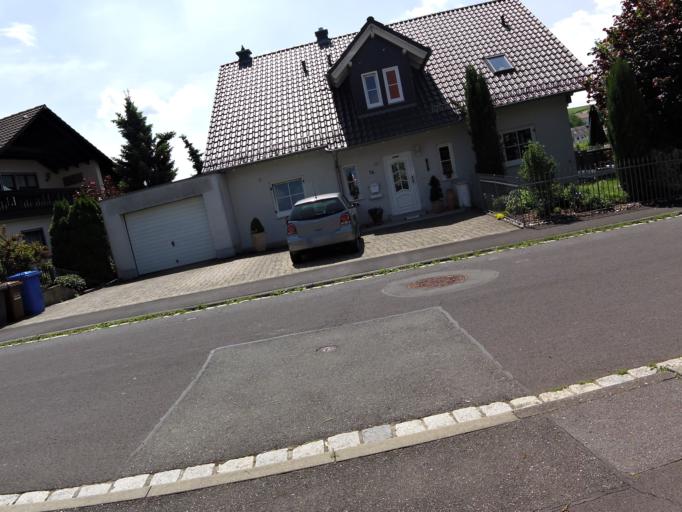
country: DE
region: Bavaria
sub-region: Regierungsbezirk Unterfranken
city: Eisingen
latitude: 49.7615
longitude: 9.8265
